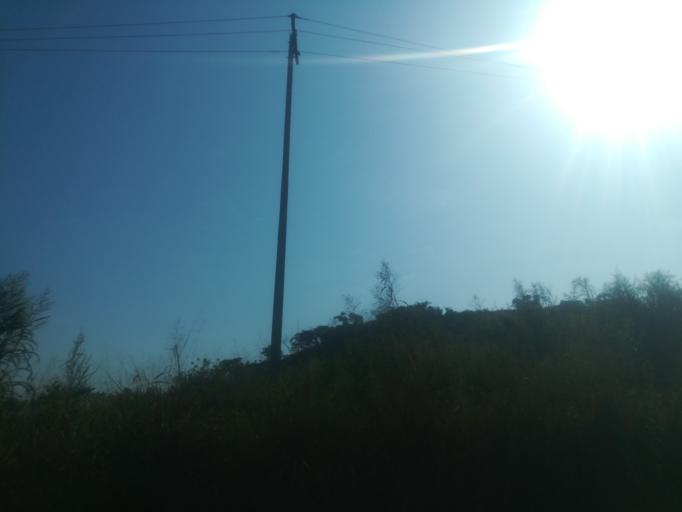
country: NG
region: Ogun
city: Abeokuta
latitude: 7.1378
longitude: 3.2793
